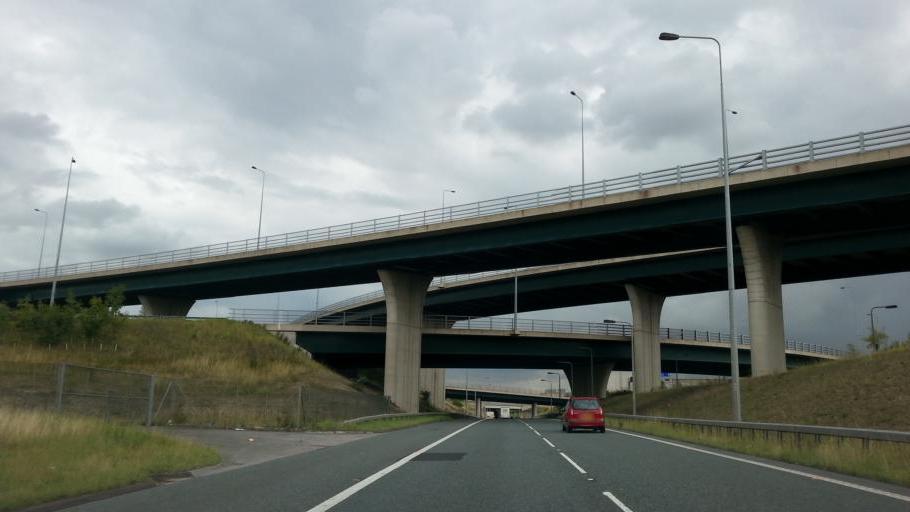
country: GB
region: England
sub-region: City and Borough of Wakefield
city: Ferrybridge
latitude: 53.7118
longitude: -1.2923
